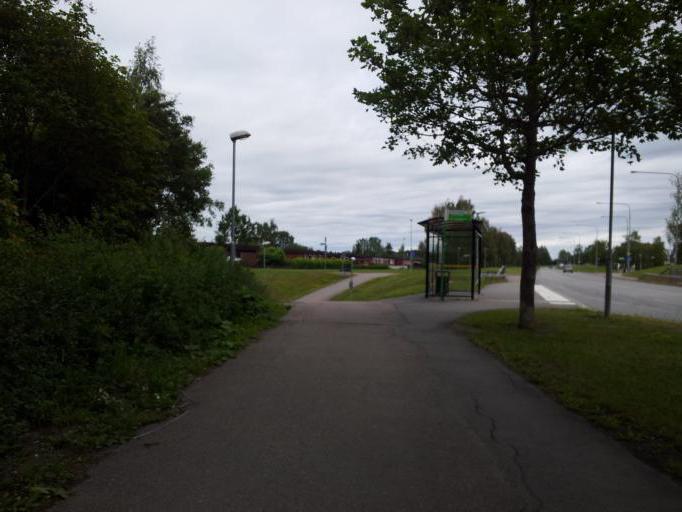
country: SE
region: Uppsala
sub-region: Uppsala Kommun
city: Gamla Uppsala
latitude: 59.8857
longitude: 17.6429
